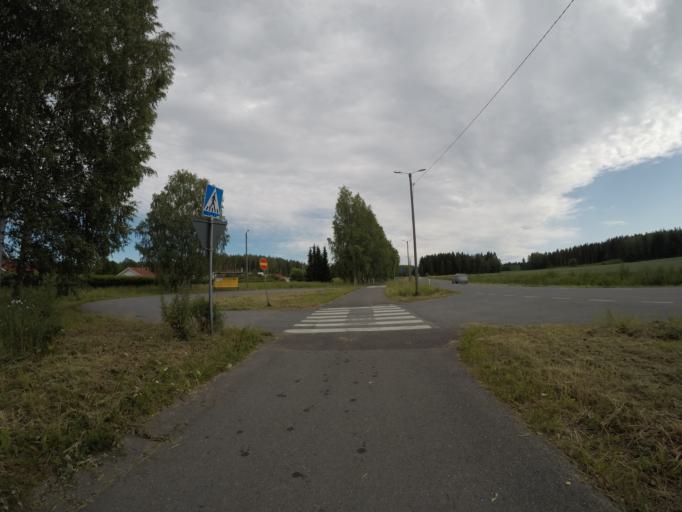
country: FI
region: Haeme
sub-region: Haemeenlinna
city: Parola
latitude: 61.0021
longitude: 24.3903
